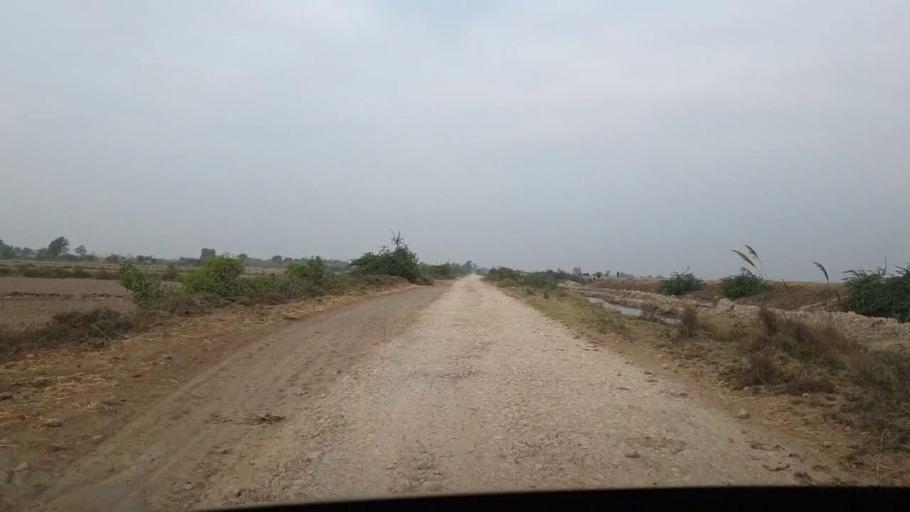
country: PK
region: Sindh
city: Chuhar Jamali
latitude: 24.4096
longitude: 67.9493
